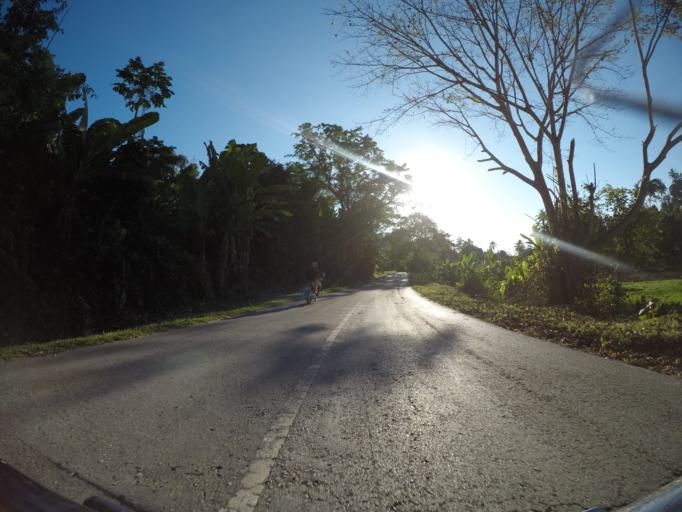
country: TZ
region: Pemba South
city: Mtambile
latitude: -5.3766
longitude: 39.6924
